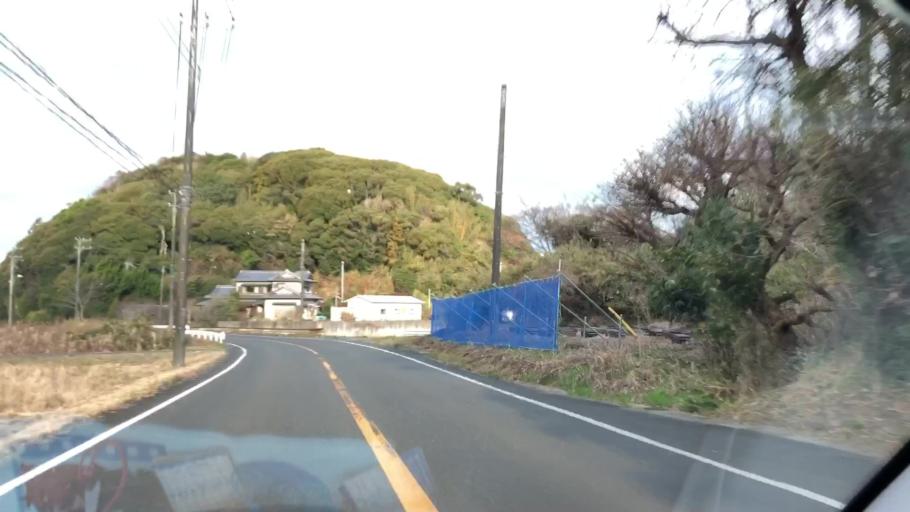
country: JP
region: Chiba
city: Tateyama
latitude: 34.9898
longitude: 139.9271
